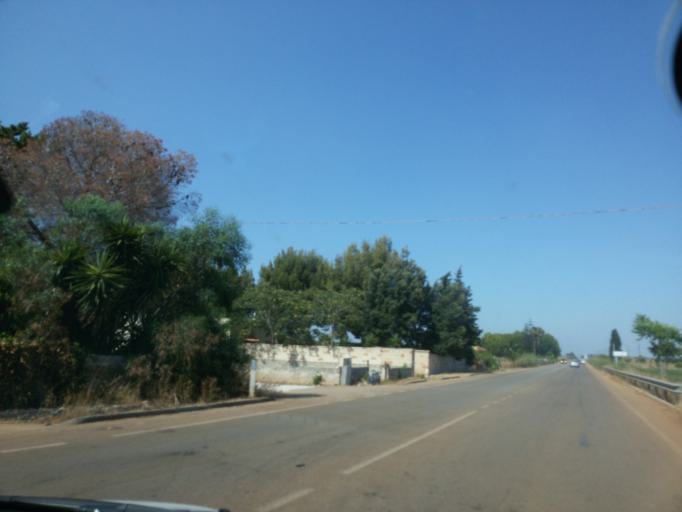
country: IT
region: Apulia
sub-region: Provincia di Lecce
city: Porto Cesareo
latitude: 40.2303
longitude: 17.9499
